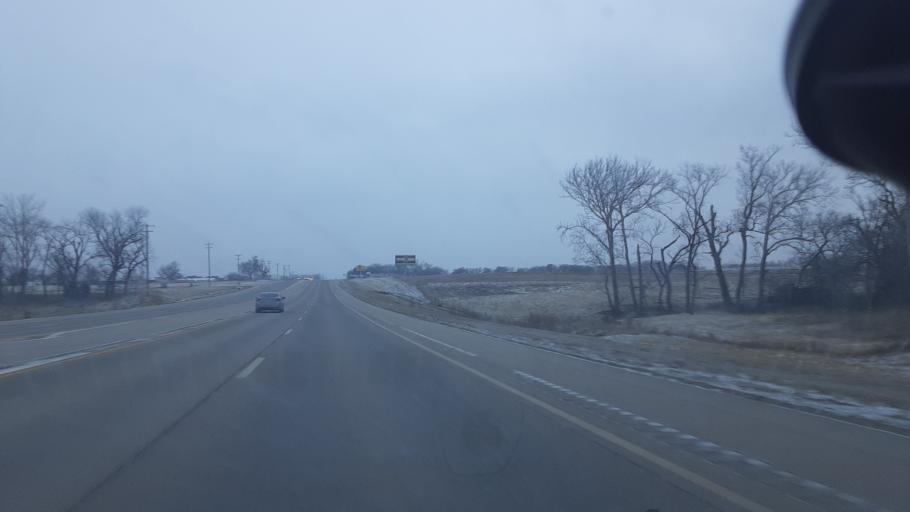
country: US
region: Oklahoma
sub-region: Payne County
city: Perkins
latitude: 35.9855
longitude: -97.0819
